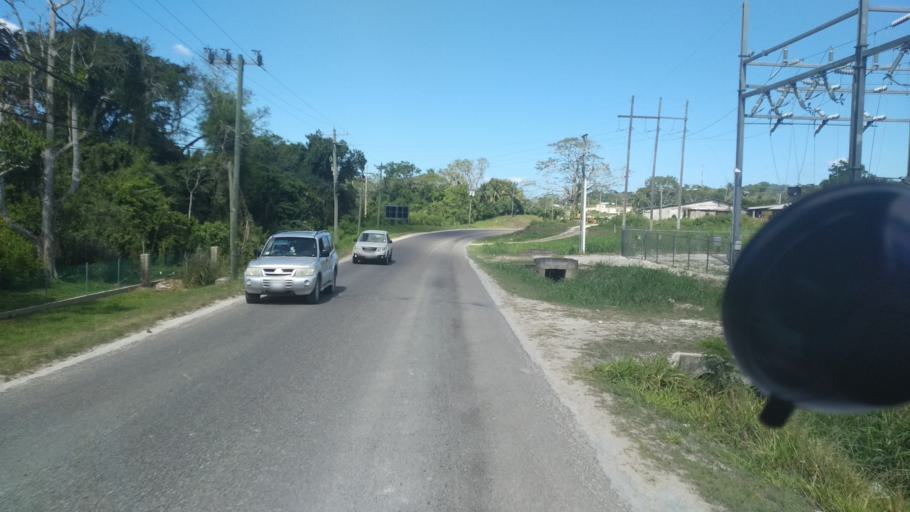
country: BZ
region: Cayo
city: San Ignacio
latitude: 17.1420
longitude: -89.0859
